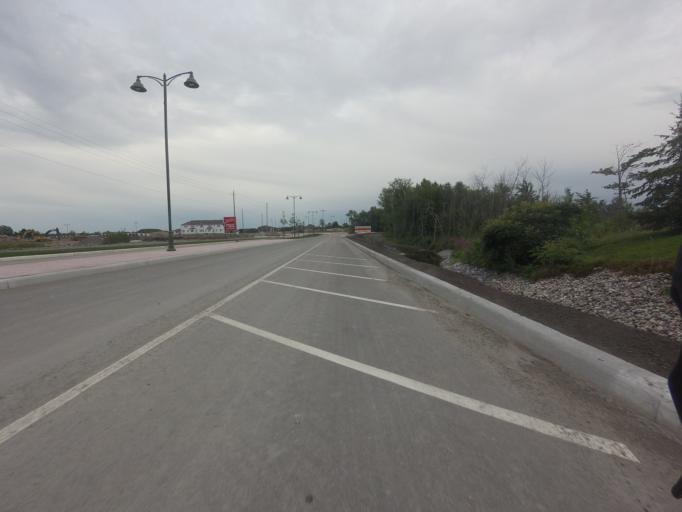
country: CA
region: Ontario
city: Carleton Place
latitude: 45.1301
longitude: -76.1177
